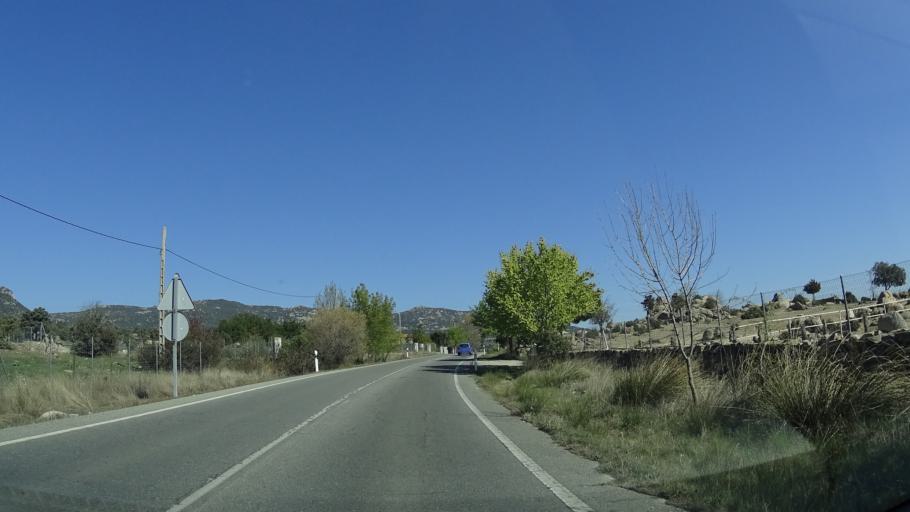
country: ES
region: Madrid
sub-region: Provincia de Madrid
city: Hoyo de Manzanares
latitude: 40.6078
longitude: -3.9040
